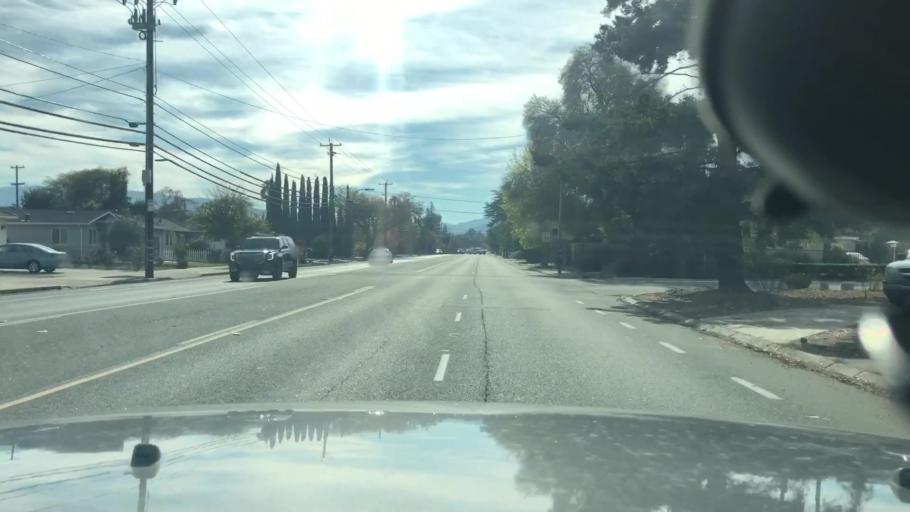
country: US
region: California
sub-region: Santa Clara County
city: Saratoga
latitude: 37.2829
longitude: -121.9944
